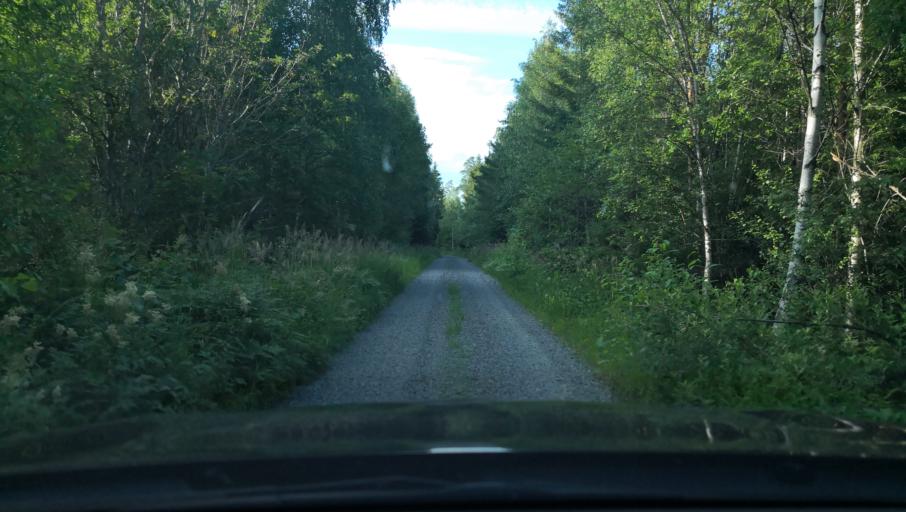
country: SE
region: Uppsala
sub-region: Osthammars Kommun
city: Osterbybruk
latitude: 60.0233
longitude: 17.9192
